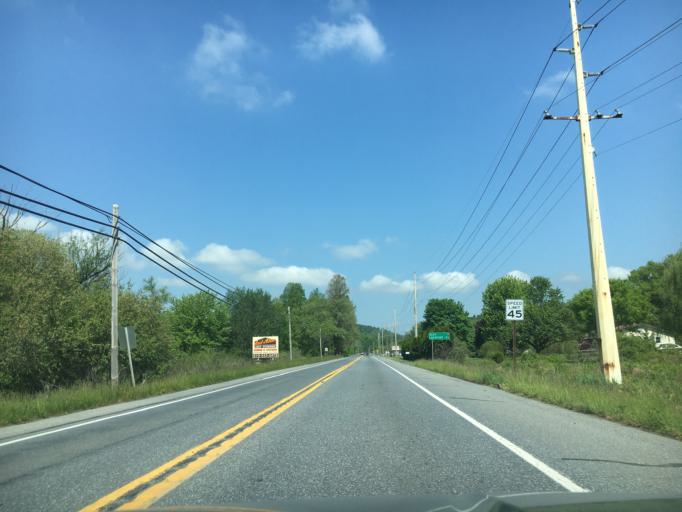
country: US
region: Pennsylvania
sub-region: Berks County
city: Boyertown
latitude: 40.3345
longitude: -75.6521
